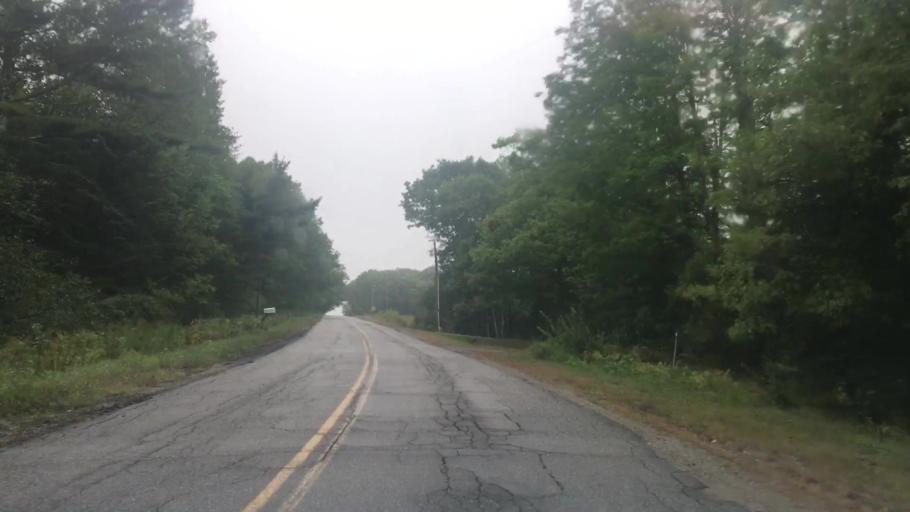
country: US
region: Maine
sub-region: Waldo County
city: Stockton Springs
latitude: 44.5413
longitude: -68.9116
